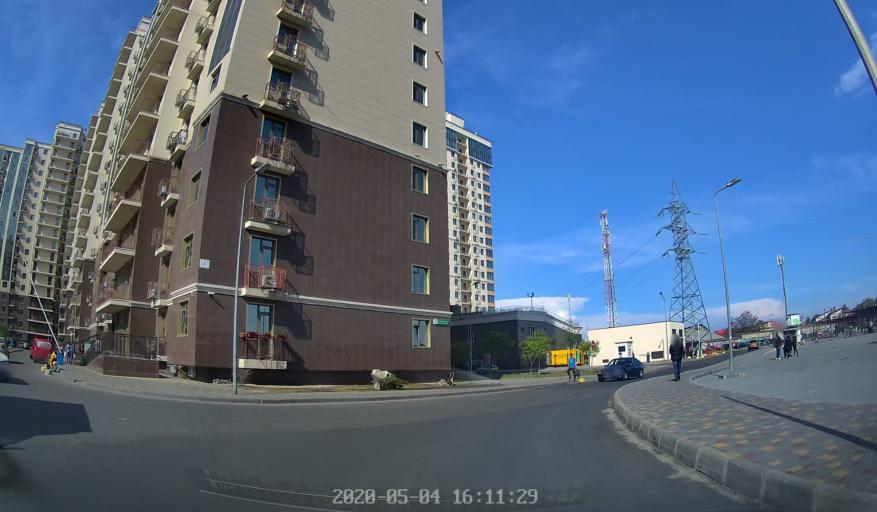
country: GR
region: South Aegean
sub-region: Nomos Kykladon
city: Serifos
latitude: 37.1053
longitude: 24.5674
